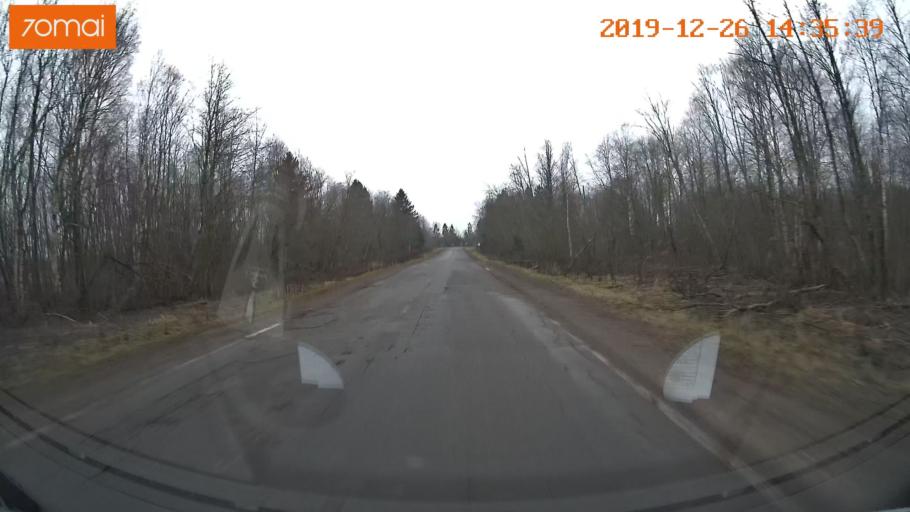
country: RU
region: Jaroslavl
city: Poshekhon'ye
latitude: 58.4185
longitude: 38.9817
